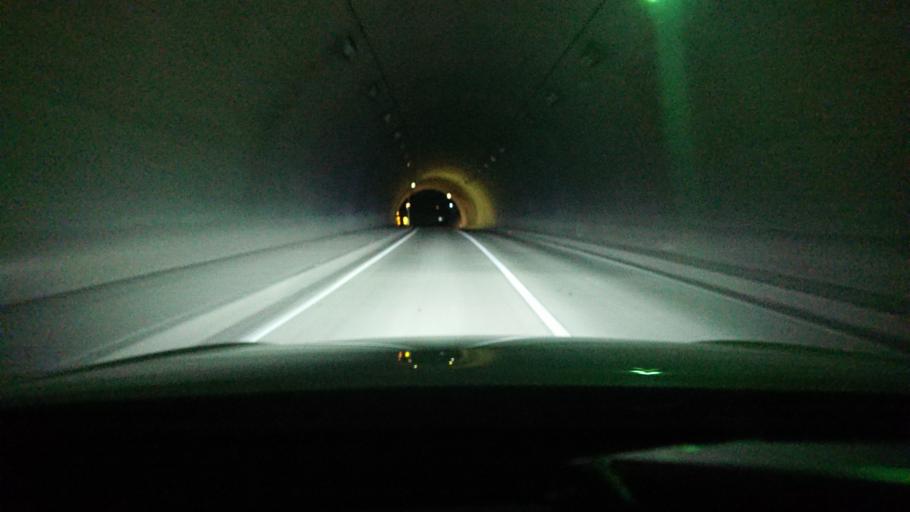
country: JP
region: Tokushima
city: Ishii
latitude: 33.9211
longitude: 134.4307
